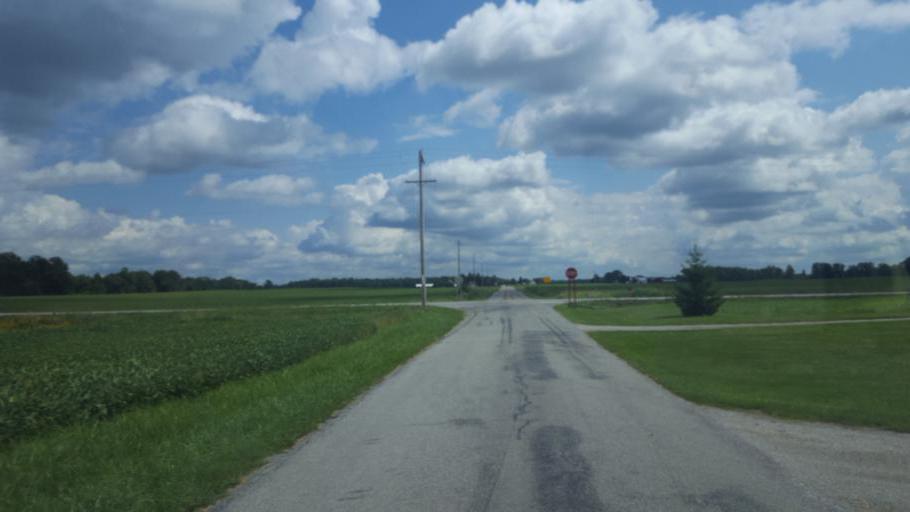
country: US
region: Ohio
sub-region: Huron County
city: Monroeville
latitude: 41.1759
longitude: -82.7255
